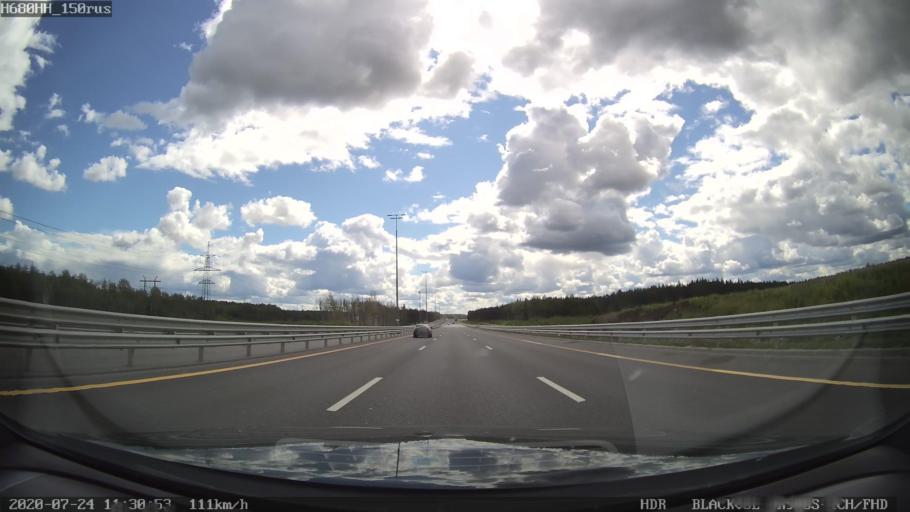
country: RU
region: Leningrad
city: Krasnyy Bor
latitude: 59.6646
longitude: 30.6220
